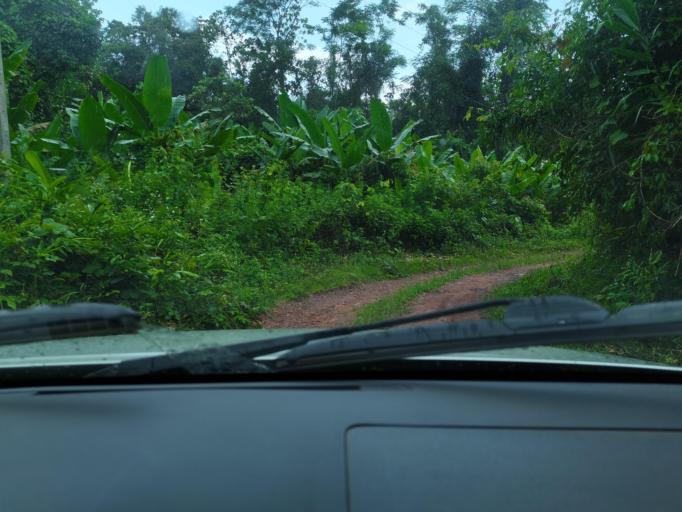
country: LA
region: Loungnamtha
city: Muang Nale
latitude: 20.5178
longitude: 101.0704
